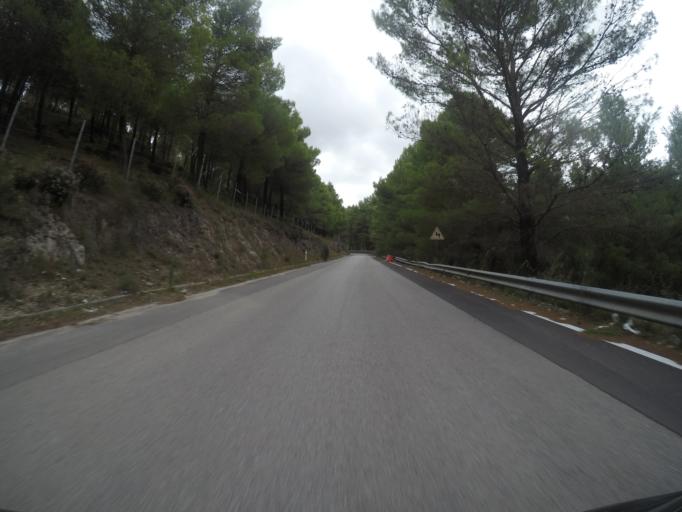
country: IT
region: Sicily
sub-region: Palermo
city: Montelepre
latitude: 38.1072
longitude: 13.1690
